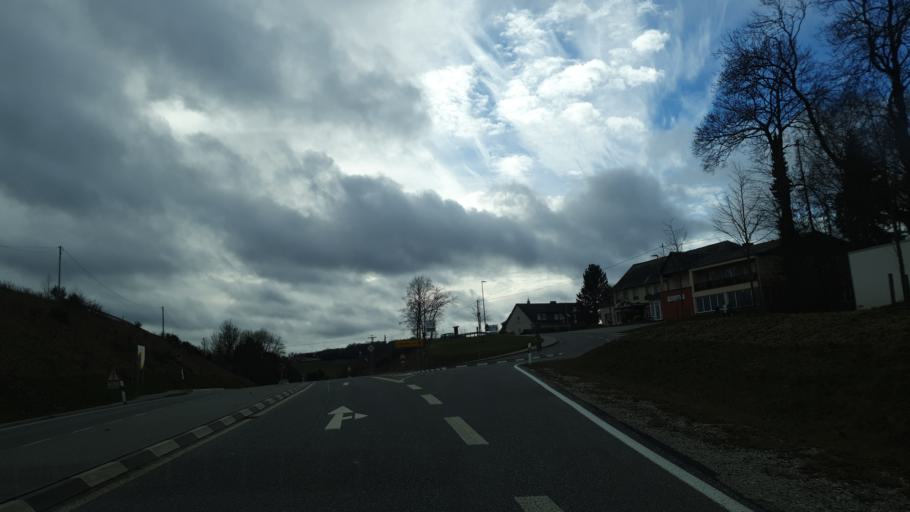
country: DE
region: Rheinland-Pfalz
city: Kratzenburg
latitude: 50.1806
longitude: 7.5703
